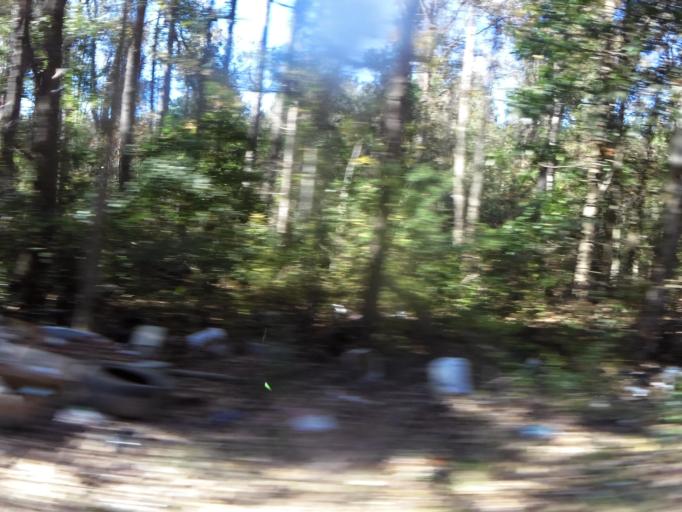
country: US
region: Georgia
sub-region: Chatham County
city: Savannah
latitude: 32.0709
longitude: -81.1412
